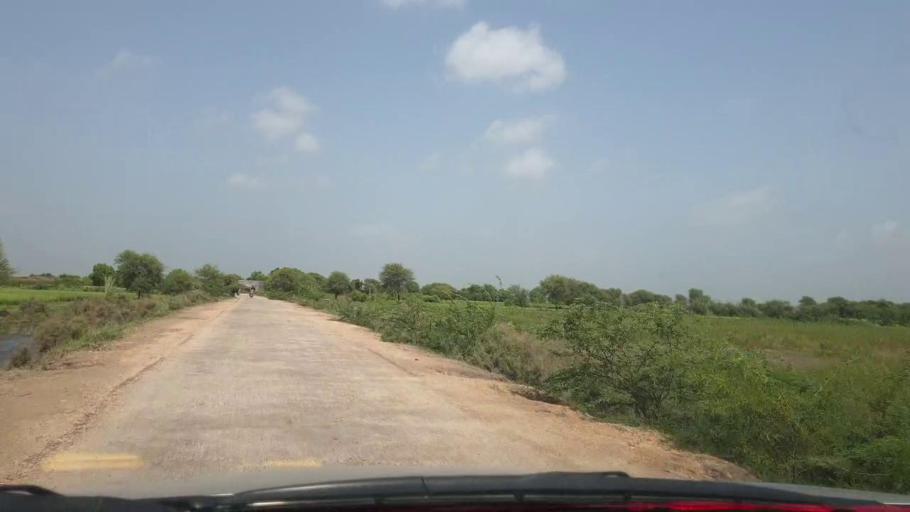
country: PK
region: Sindh
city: Tando Bago
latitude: 24.8729
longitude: 68.9277
